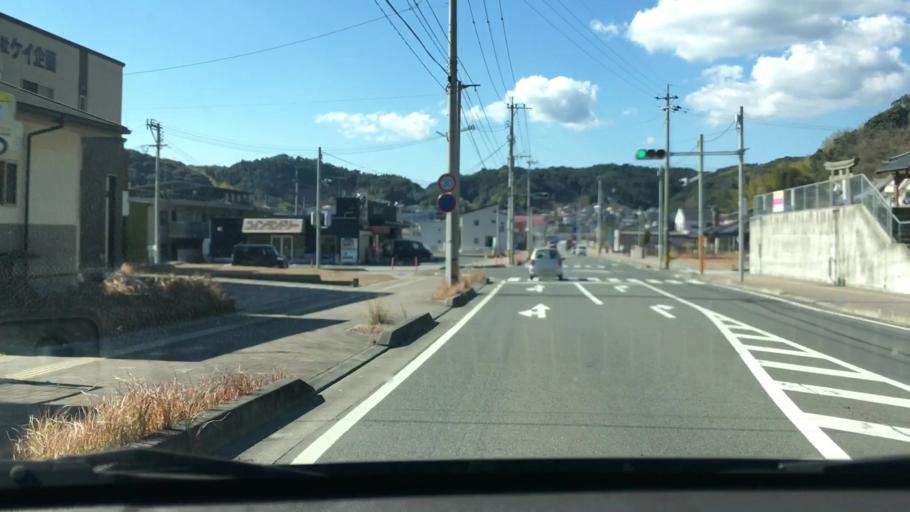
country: JP
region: Kagoshima
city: Ijuin
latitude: 31.6805
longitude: 130.4742
